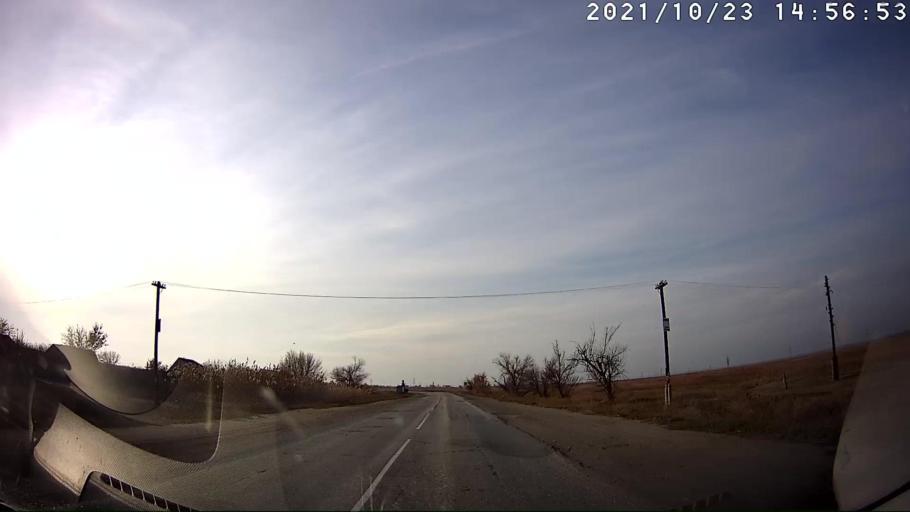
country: RU
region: Volgograd
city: Volgograd
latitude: 48.4572
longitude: 44.3749
